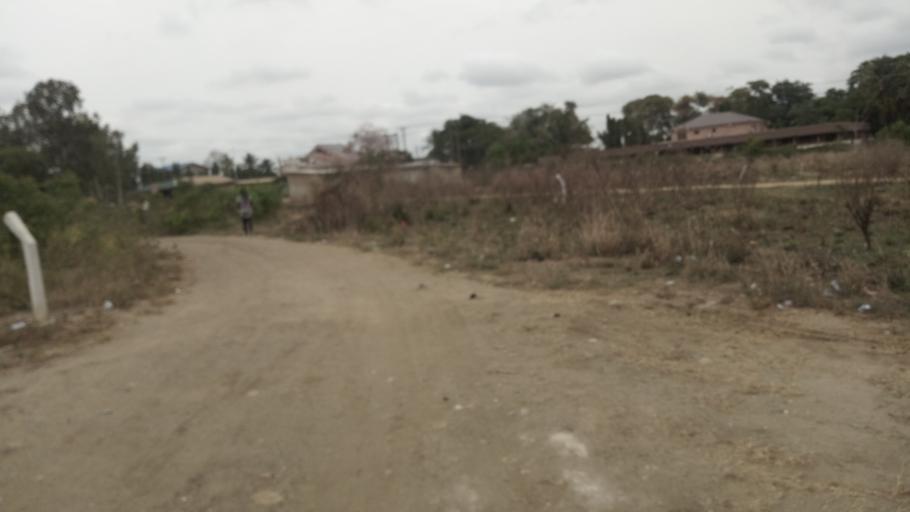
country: GH
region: Central
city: Winneba
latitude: 5.3654
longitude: -0.6382
